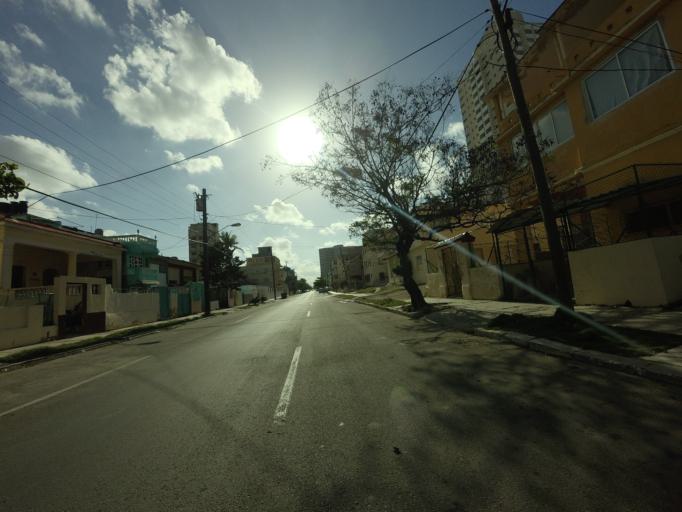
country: CU
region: La Habana
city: Havana
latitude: 23.1426
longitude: -82.3979
